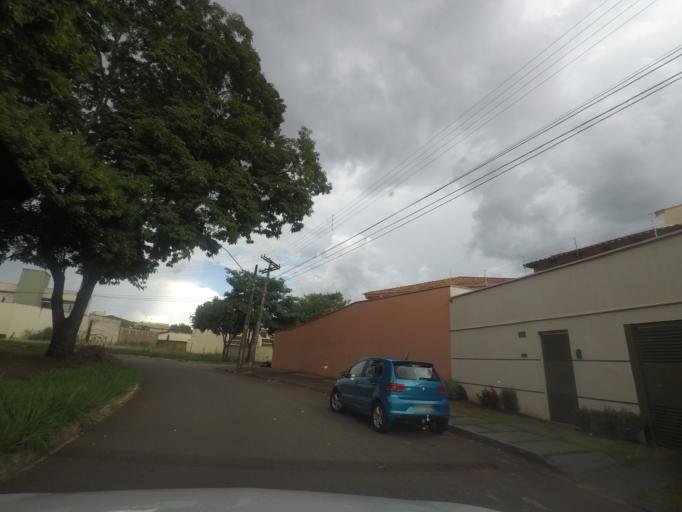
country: BR
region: Goias
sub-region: Goiania
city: Goiania
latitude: -16.6395
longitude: -49.2288
